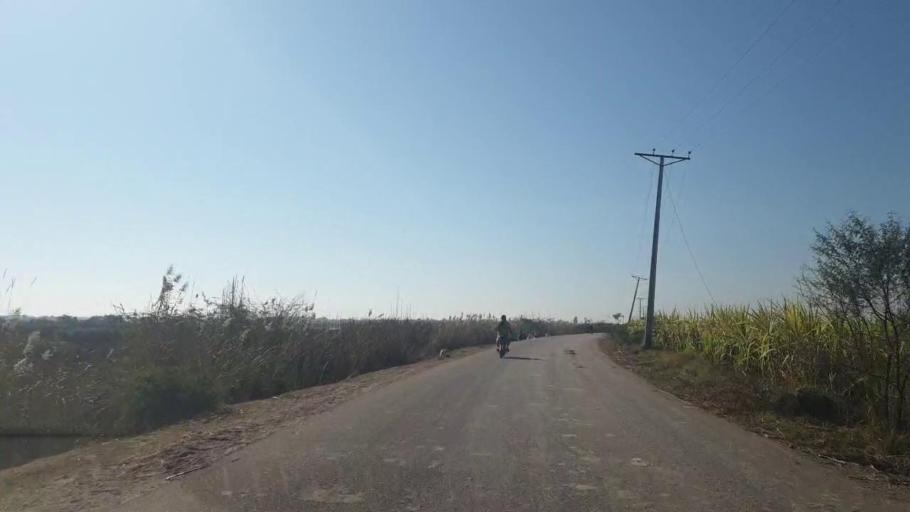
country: PK
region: Sindh
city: Kot Diji
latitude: 27.3059
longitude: 68.6458
